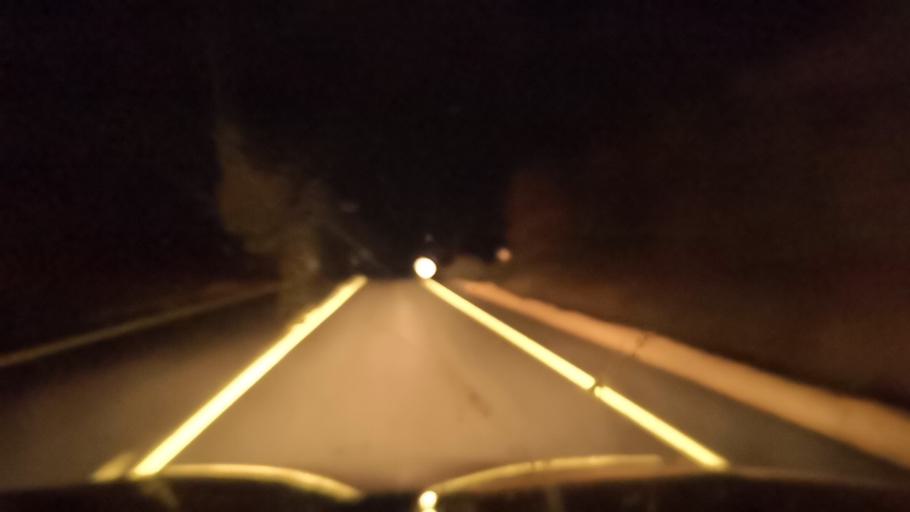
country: ES
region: Castille and Leon
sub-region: Provincia de Salamanca
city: Villasrubias
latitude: 40.3612
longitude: -6.6237
